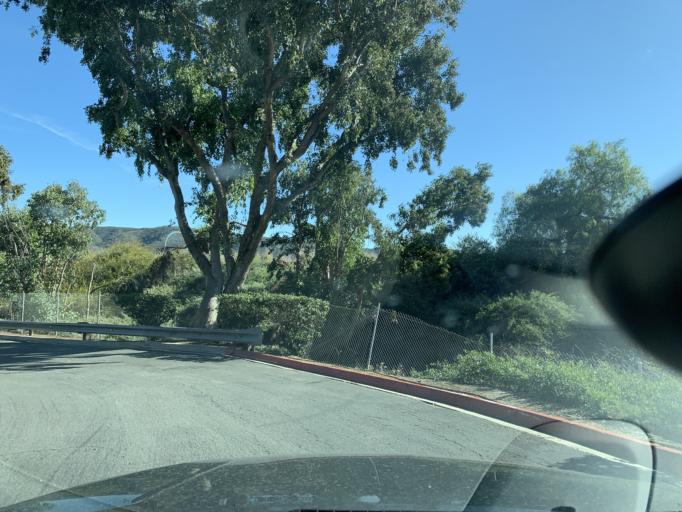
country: US
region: California
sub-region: San Diego County
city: Poway
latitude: 32.9638
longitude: -117.1004
